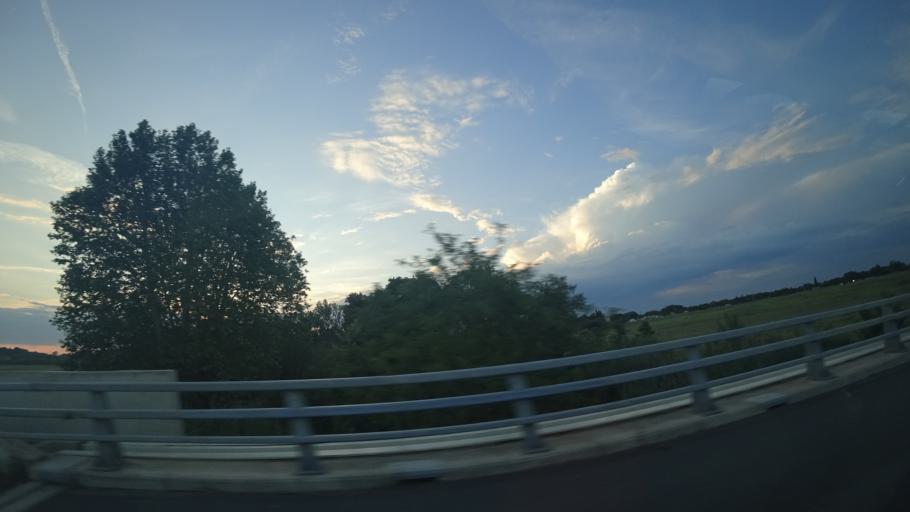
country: FR
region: Languedoc-Roussillon
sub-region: Departement de l'Herault
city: Boujan-sur-Libron
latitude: 43.3700
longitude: 3.2834
